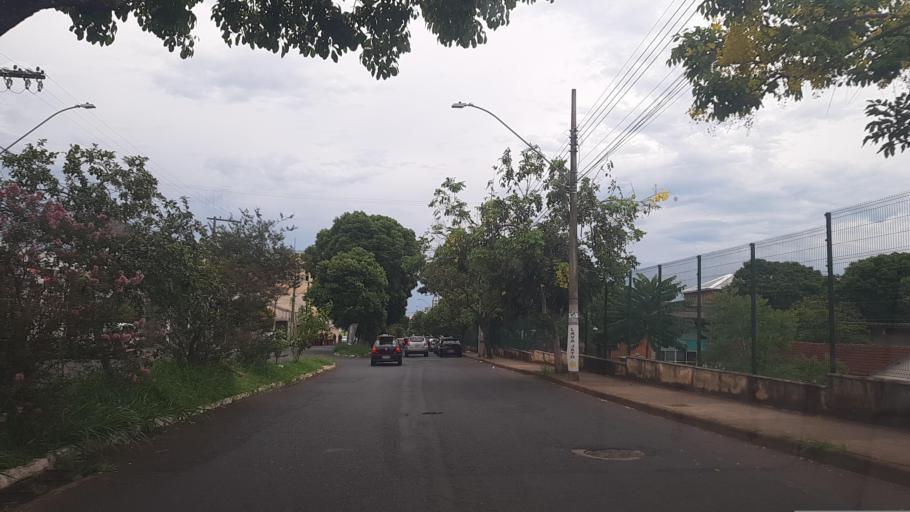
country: BR
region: Minas Gerais
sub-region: Uberlandia
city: Uberlandia
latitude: -18.9203
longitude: -48.2590
